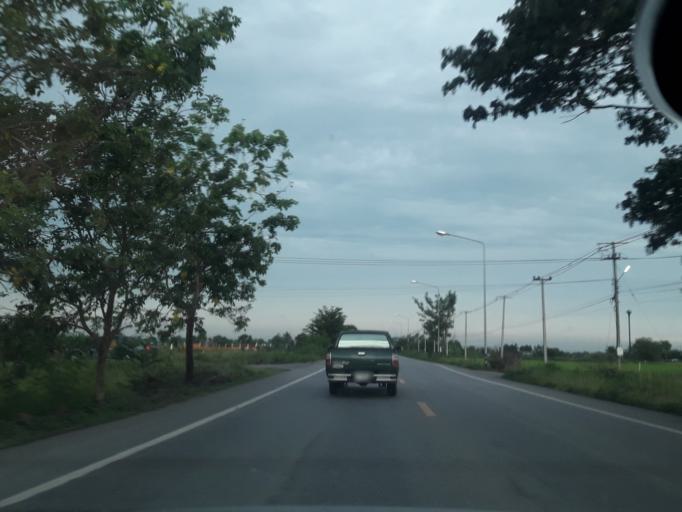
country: TH
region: Phra Nakhon Si Ayutthaya
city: Wang Noi
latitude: 14.1607
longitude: 100.7474
